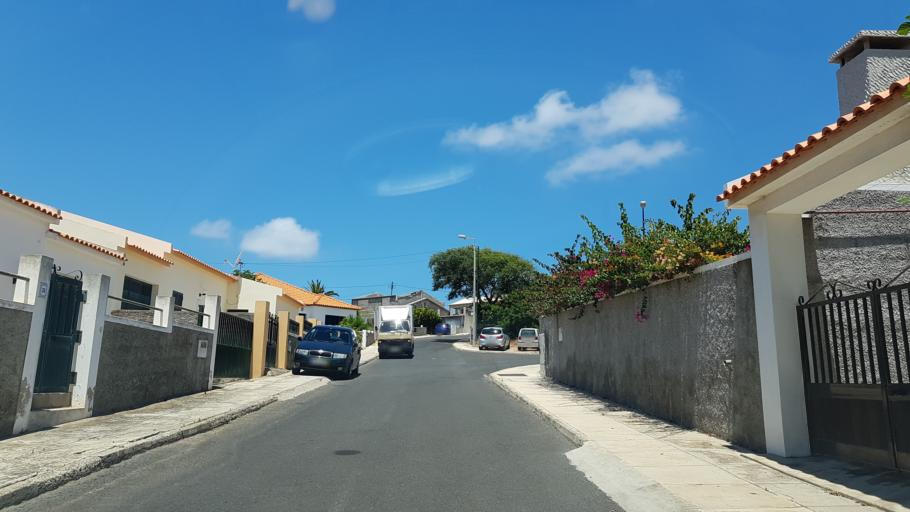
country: PT
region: Madeira
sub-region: Porto Santo
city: Vila de Porto Santo
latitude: 33.0581
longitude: -16.3537
